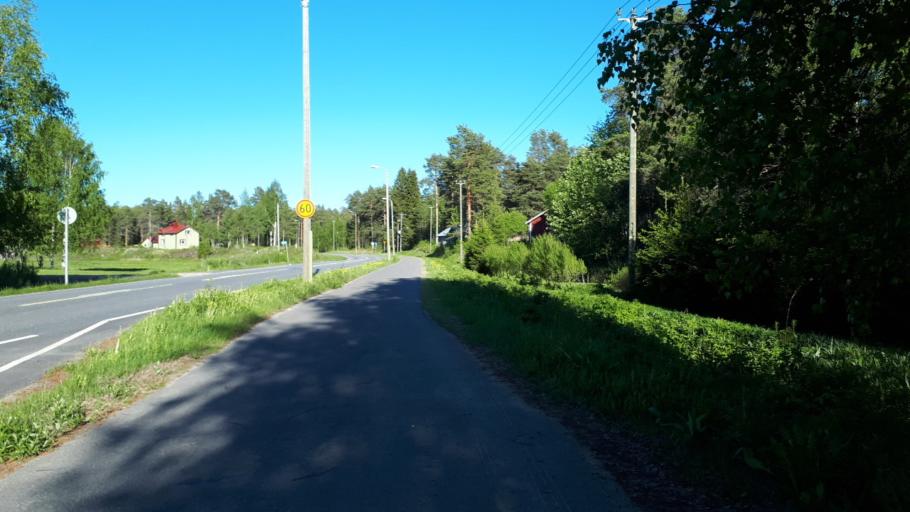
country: FI
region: Northern Ostrobothnia
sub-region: Oulunkaari
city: Ii
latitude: 65.3223
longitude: 25.4569
